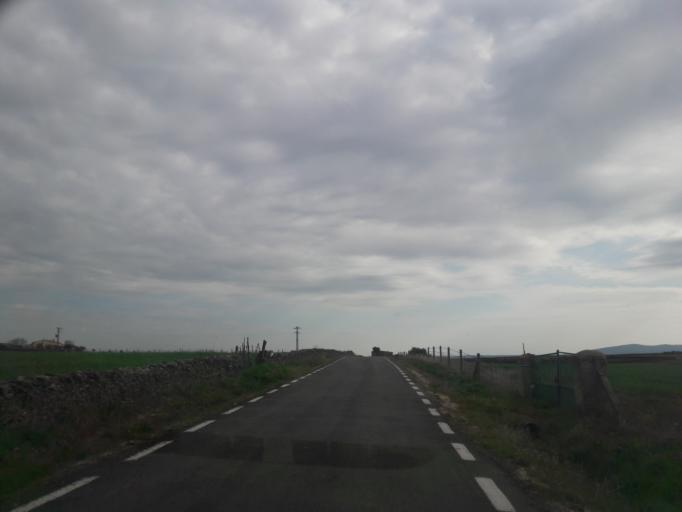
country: ES
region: Castille and Leon
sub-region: Provincia de Salamanca
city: Pastores
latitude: 40.5021
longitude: -6.5248
